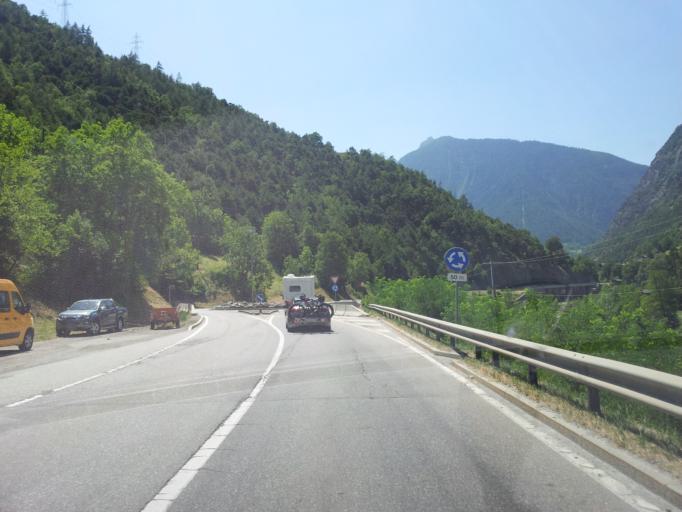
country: CH
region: Valais
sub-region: Visp District
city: Visperterminen
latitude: 46.2582
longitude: 7.8798
